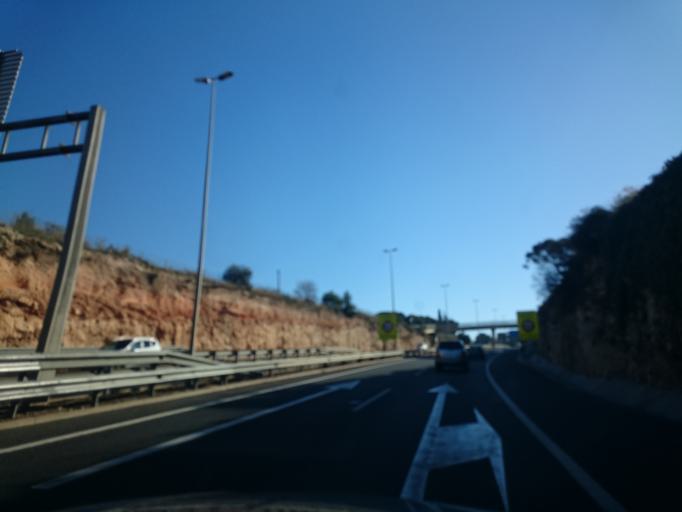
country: ES
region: Catalonia
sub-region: Provincia de Tarragona
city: Tarragona
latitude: 41.1264
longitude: 1.2428
